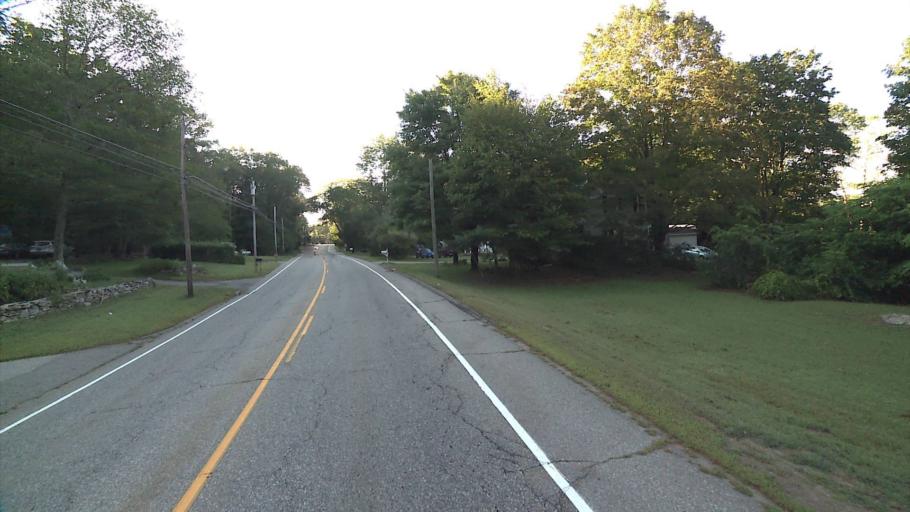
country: US
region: Connecticut
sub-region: Tolland County
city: Mansfield City
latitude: 41.7590
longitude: -72.2657
